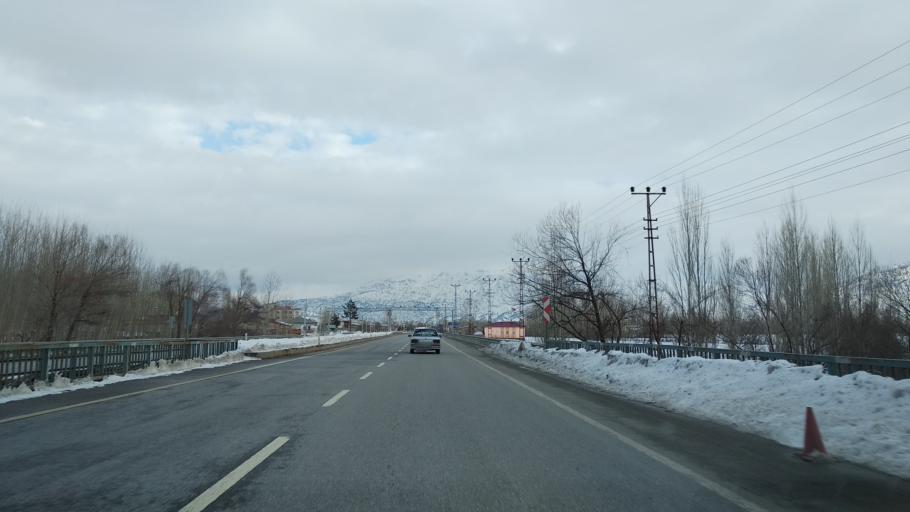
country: TR
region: Kahramanmaras
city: Goksun
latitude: 38.0321
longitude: 36.4720
